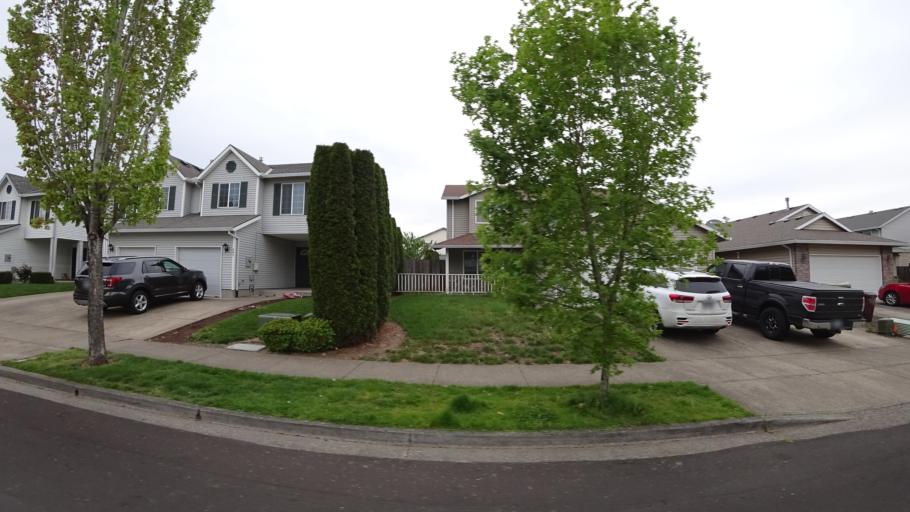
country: US
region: Oregon
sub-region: Washington County
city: Aloha
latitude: 45.5152
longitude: -122.9073
